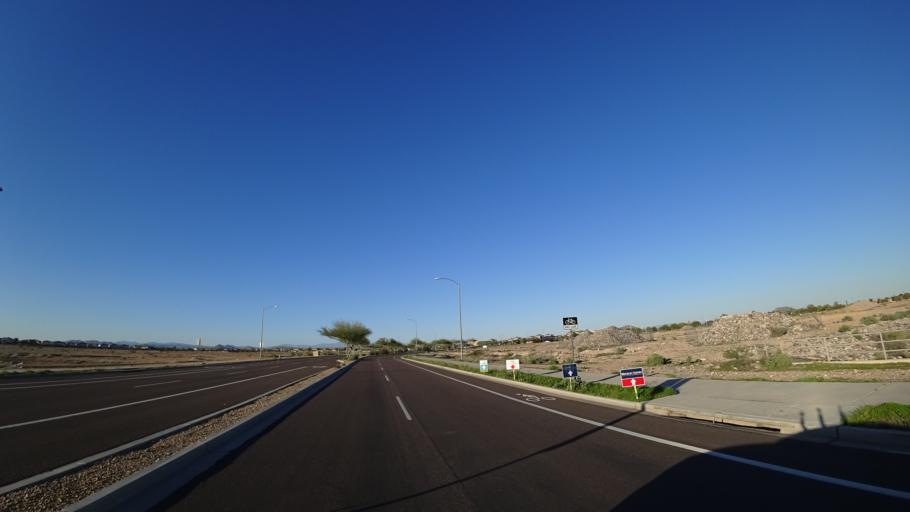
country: US
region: Arizona
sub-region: Maricopa County
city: Sun City West
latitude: 33.6746
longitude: -112.2799
